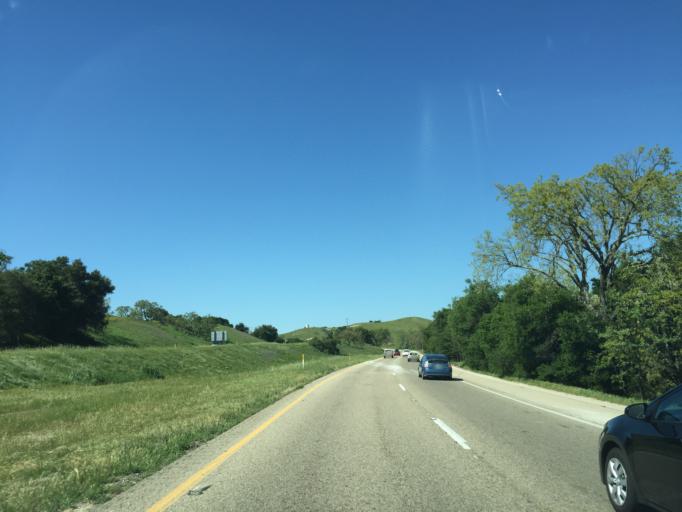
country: US
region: California
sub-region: Santa Barbara County
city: Los Olivos
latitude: 34.7022
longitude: -120.1684
